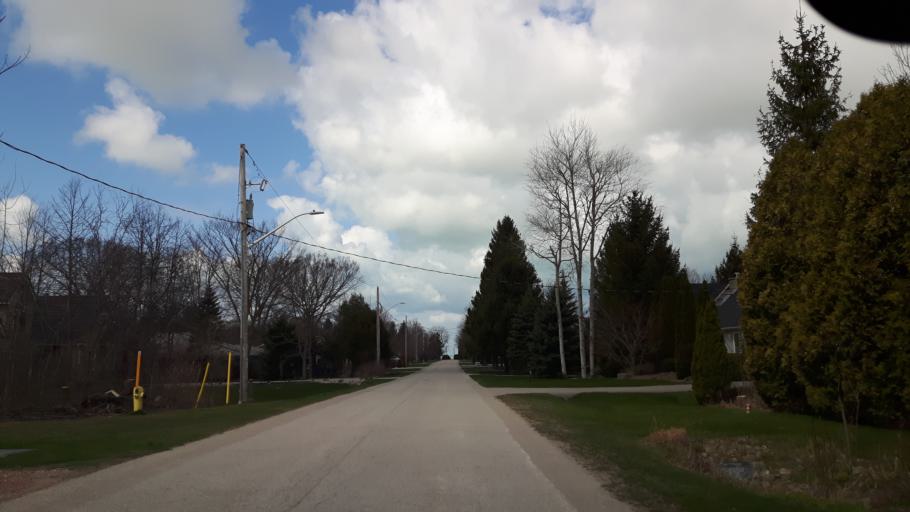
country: CA
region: Ontario
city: Bluewater
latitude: 43.5586
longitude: -81.7002
